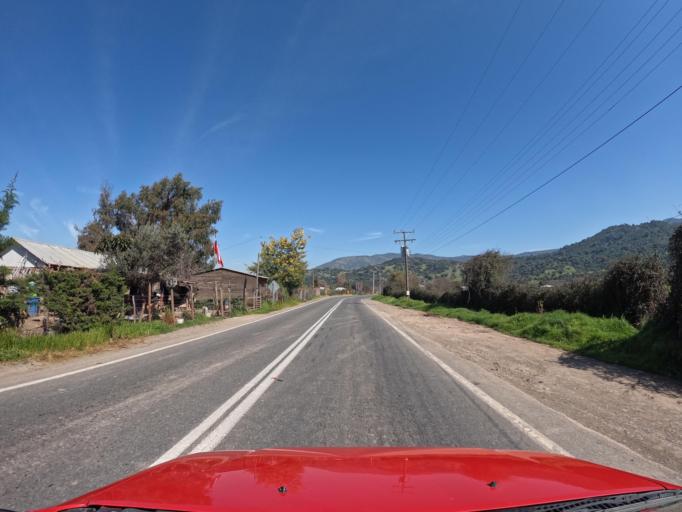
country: CL
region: Maule
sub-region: Provincia de Curico
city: Rauco
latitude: -34.9817
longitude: -71.4136
